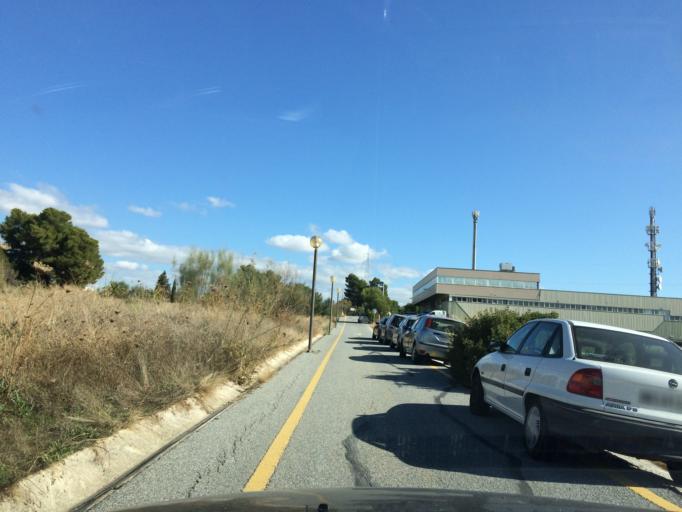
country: ES
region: Andalusia
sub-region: Provincia de Malaga
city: Estacion de Cartama
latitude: 36.7344
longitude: -4.5501
